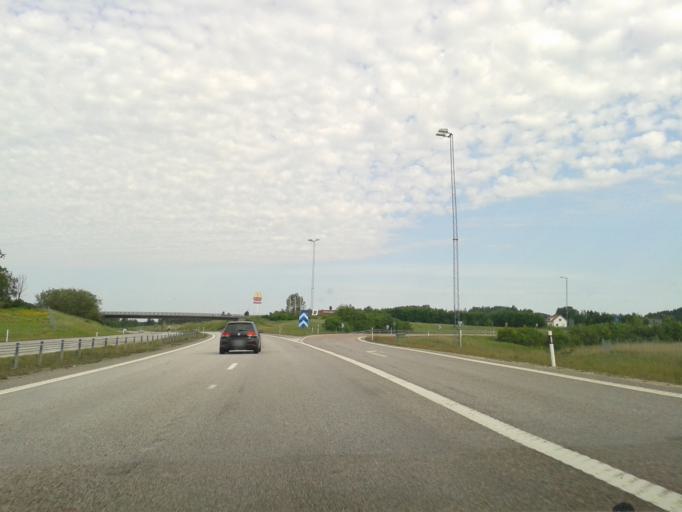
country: SE
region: Vaestra Goetaland
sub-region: Munkedals Kommun
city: Munkedal
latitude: 58.4874
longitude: 11.6267
